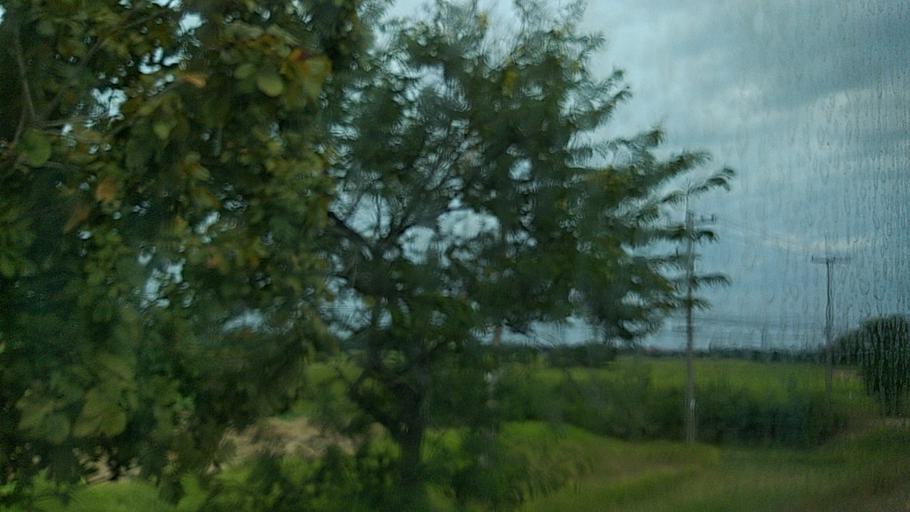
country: TH
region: Maha Sarakham
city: Maha Sarakham
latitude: 16.1506
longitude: 103.3866
